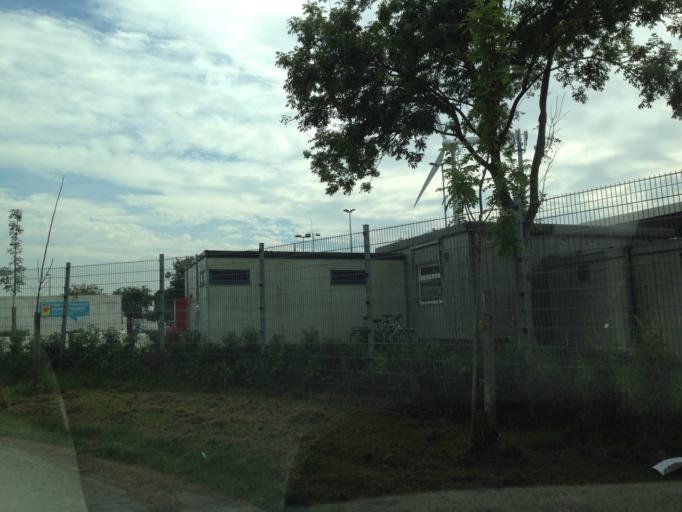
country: BE
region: Flanders
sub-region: Provincie West-Vlaanderen
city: Brugge
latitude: 51.2509
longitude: 3.2084
